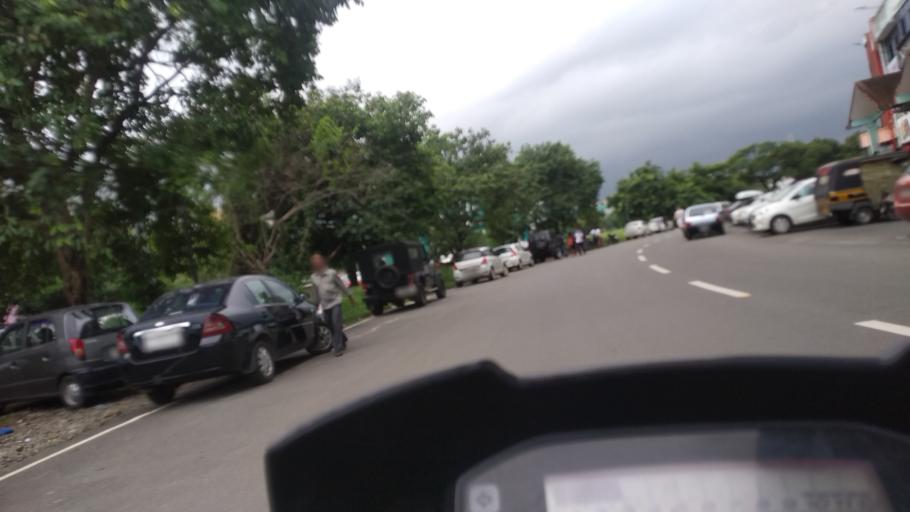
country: IN
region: Kerala
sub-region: Ernakulam
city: Cochin
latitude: 9.9971
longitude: 76.2998
